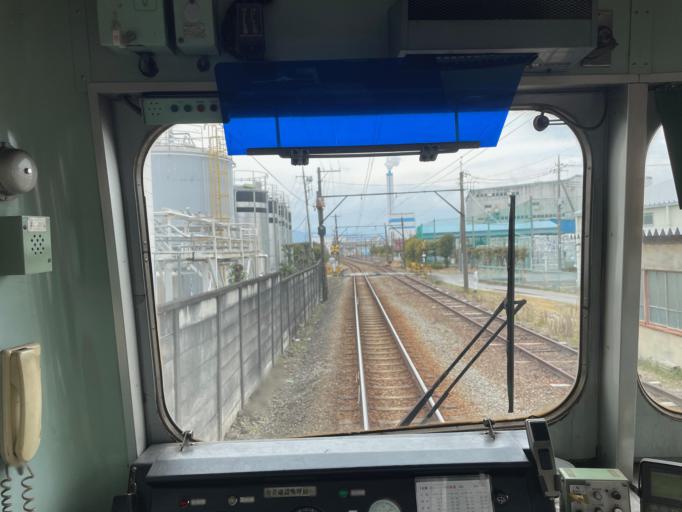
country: JP
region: Shizuoka
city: Fuji
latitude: 35.1612
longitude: 138.7202
